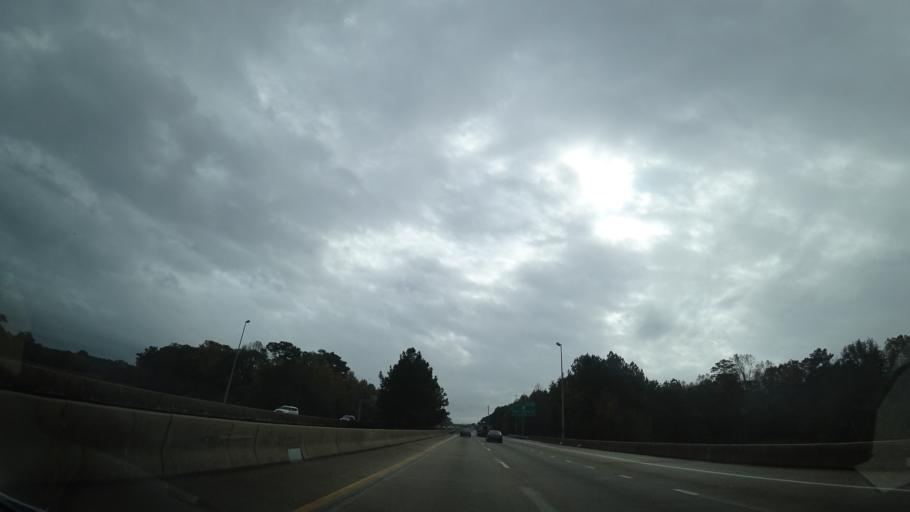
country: US
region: Virginia
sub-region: City of Portsmouth
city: Portsmouth Heights
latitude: 36.8142
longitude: -76.4318
